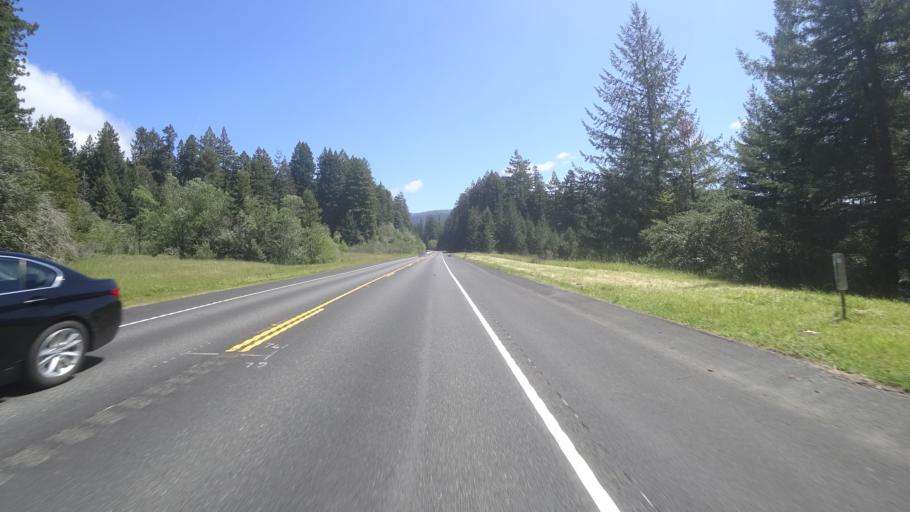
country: US
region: California
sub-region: Humboldt County
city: Blue Lake
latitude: 40.8845
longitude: -123.9592
